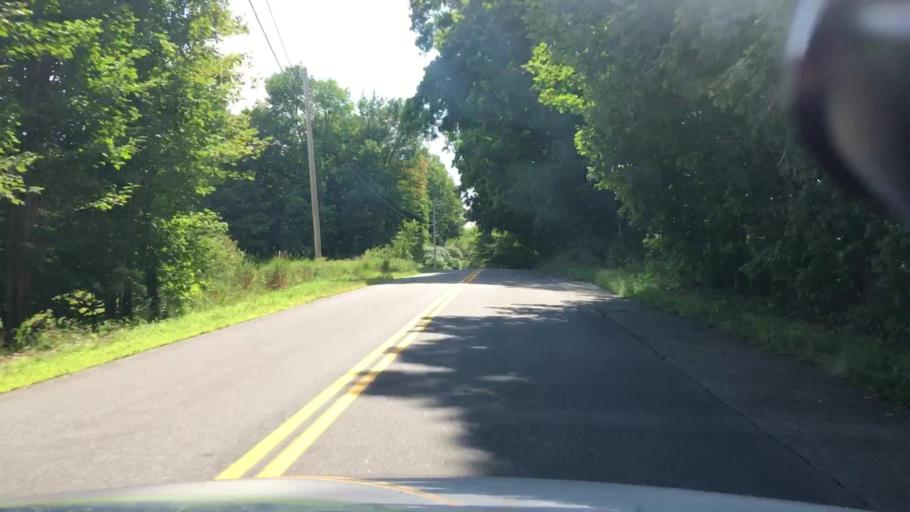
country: US
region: Maine
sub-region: Somerset County
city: Skowhegan
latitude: 44.7329
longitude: -69.7097
